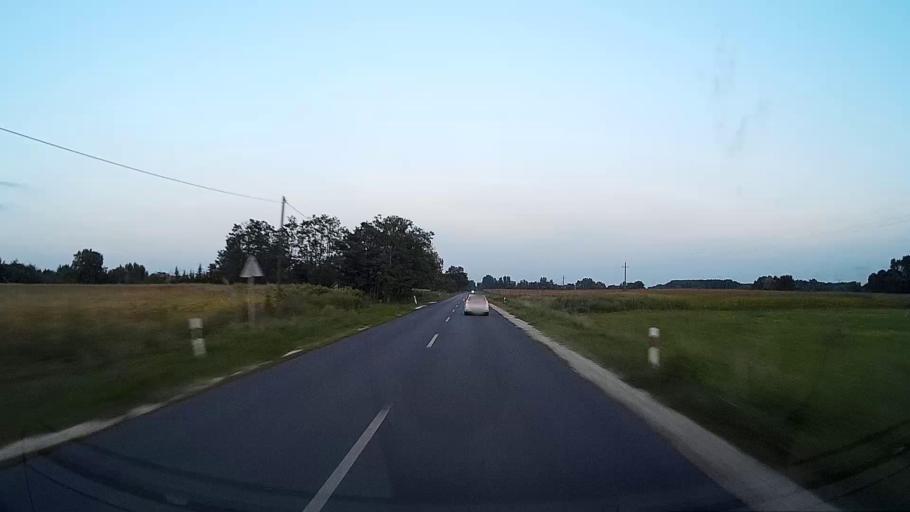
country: HU
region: Pest
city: Albertirsa
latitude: 47.2446
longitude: 19.6320
